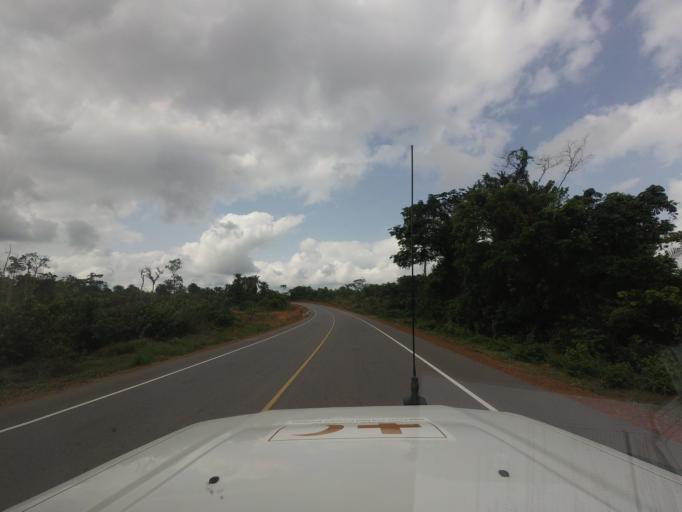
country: LR
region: Nimba
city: Sanniquellie
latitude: 7.1778
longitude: -9.0324
